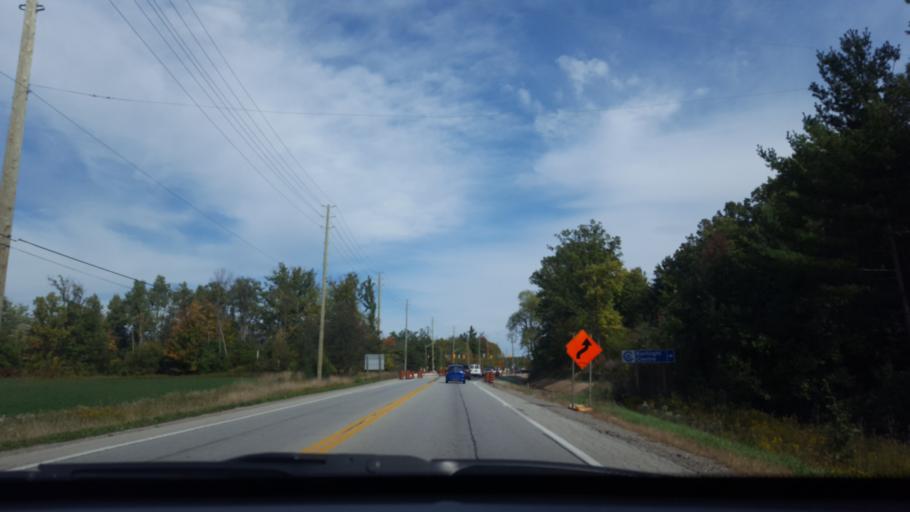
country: CA
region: Ontario
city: Vaughan
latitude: 43.8387
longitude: -79.5894
